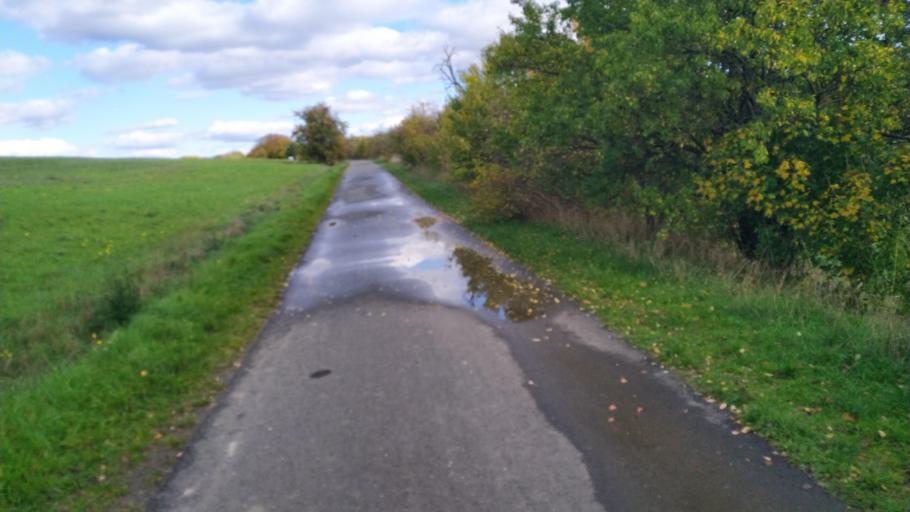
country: DE
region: Thuringia
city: Kromsdorf
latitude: 51.0035
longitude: 11.3810
